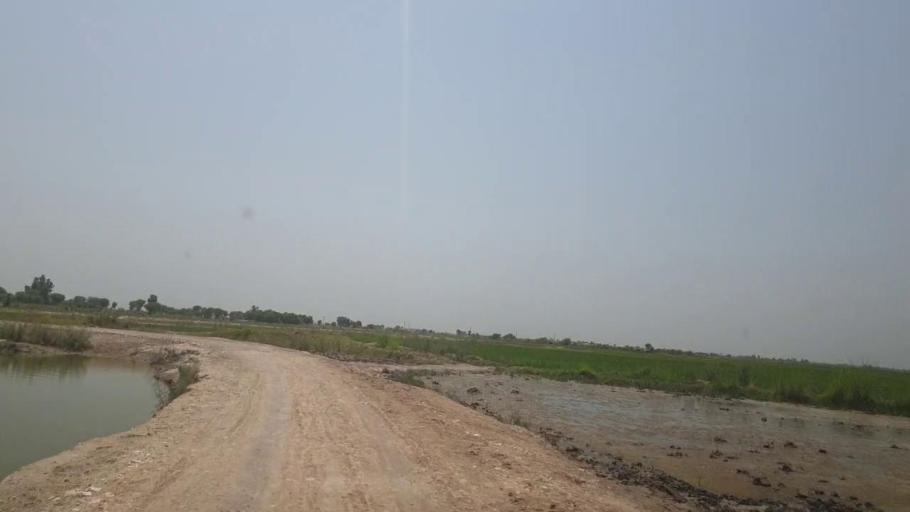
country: PK
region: Sindh
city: Lakhi
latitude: 27.8520
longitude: 68.6643
